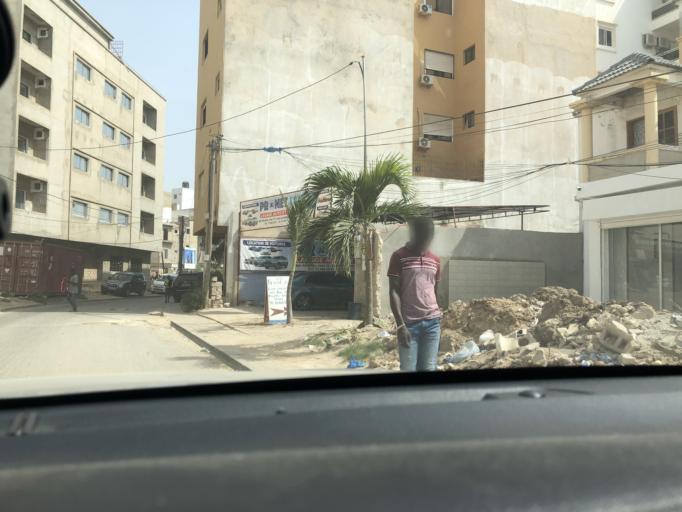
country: SN
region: Dakar
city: Mermoz Boabab
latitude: 14.7447
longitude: -17.5132
